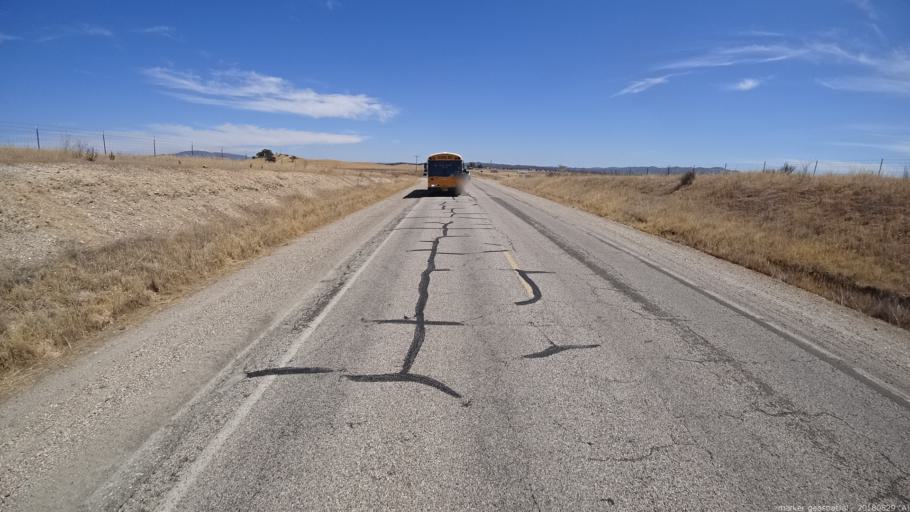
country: US
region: California
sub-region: Monterey County
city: King City
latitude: 35.9533
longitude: -121.1500
